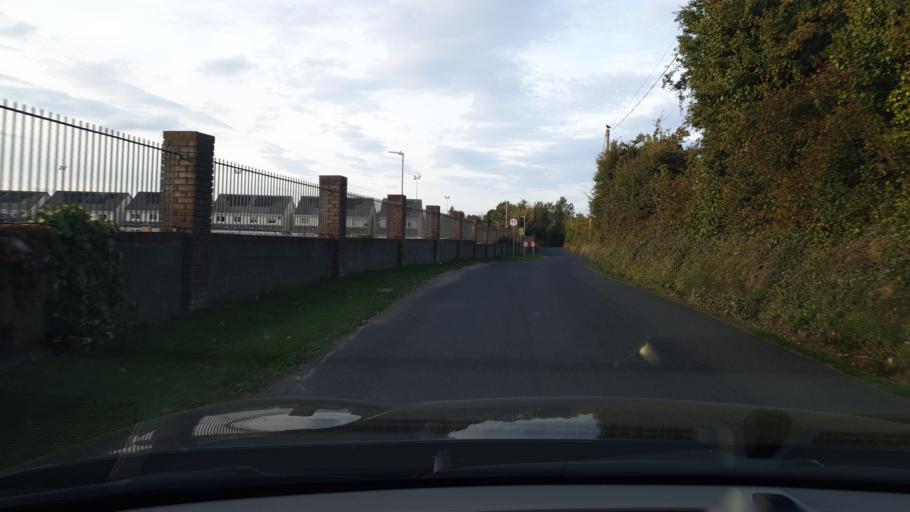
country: IE
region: Leinster
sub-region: An Mhi
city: Ashbourne
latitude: 53.5089
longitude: -6.3846
